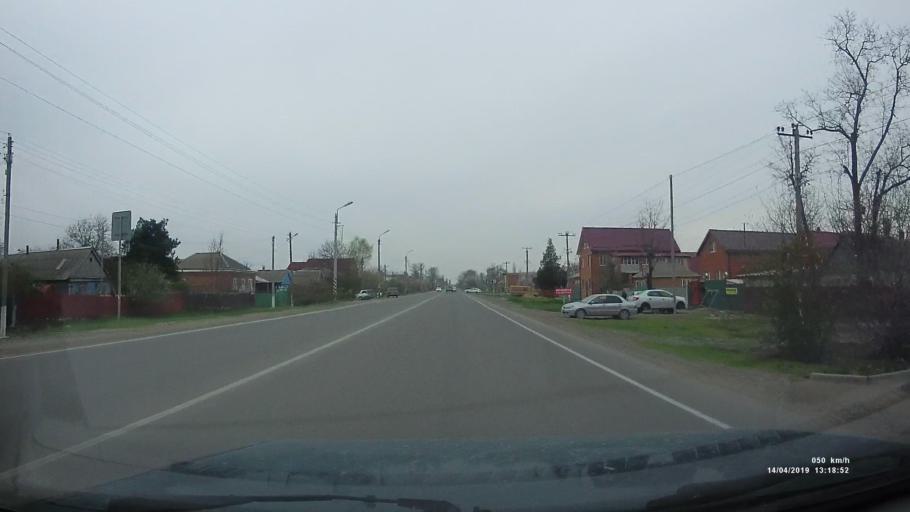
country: RU
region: Rostov
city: Kuleshovka
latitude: 47.0791
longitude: 39.5526
